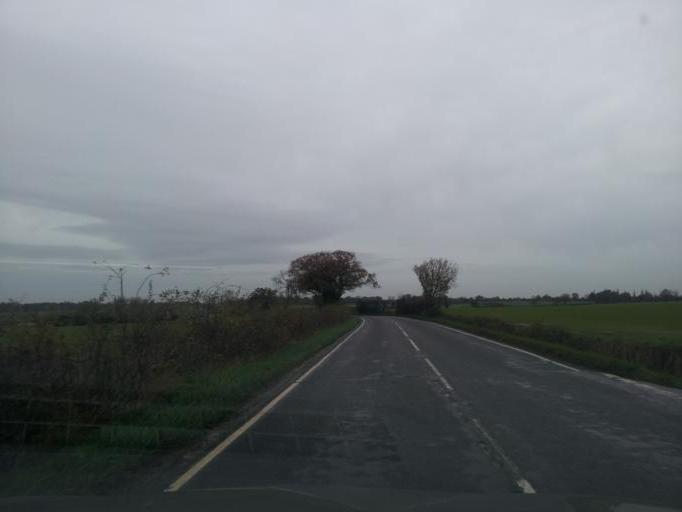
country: GB
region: England
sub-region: Essex
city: West Bergholt
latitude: 51.9315
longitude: 0.8400
